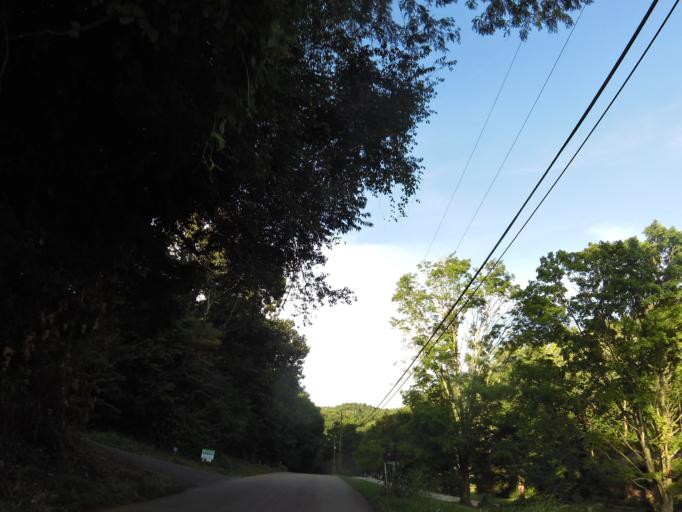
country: US
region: Tennessee
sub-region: Knox County
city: Knoxville
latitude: 35.9032
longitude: -83.9162
